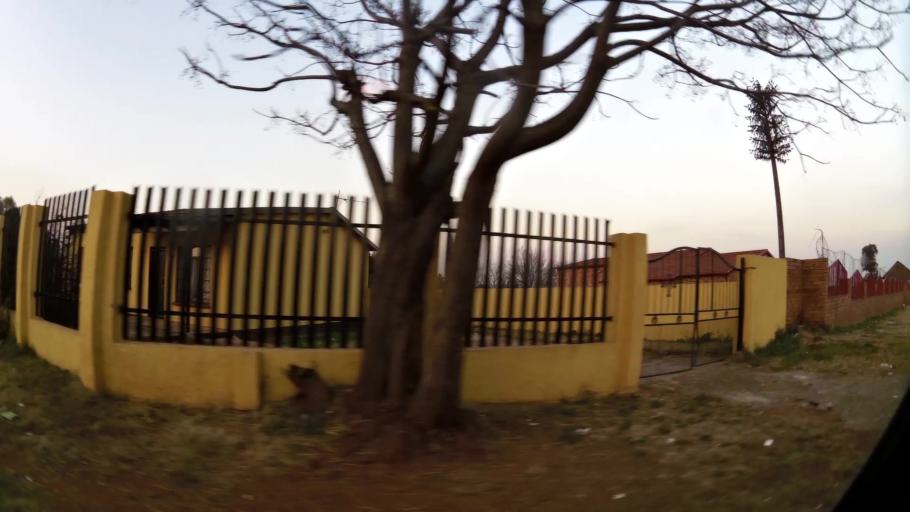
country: ZA
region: Gauteng
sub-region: City of Johannesburg Metropolitan Municipality
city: Soweto
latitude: -26.2861
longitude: 27.8775
